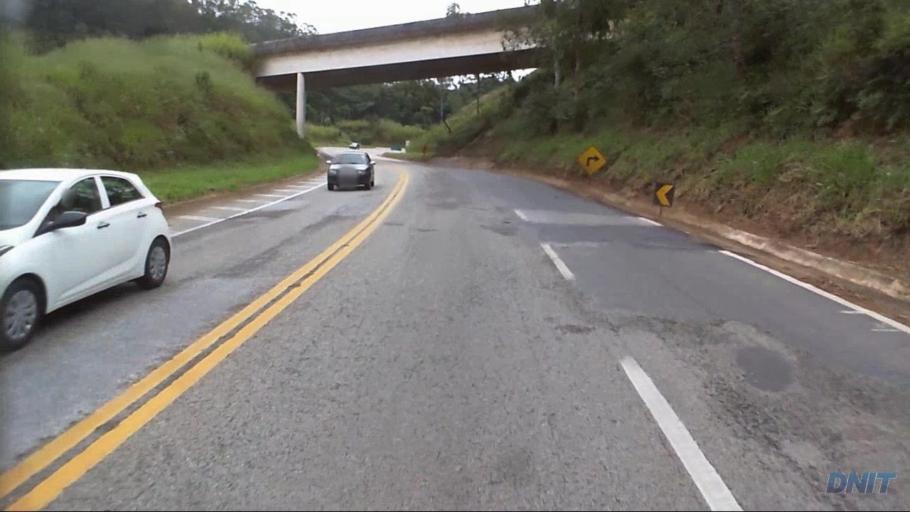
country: BR
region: Minas Gerais
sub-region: Joao Monlevade
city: Joao Monlevade
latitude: -19.8631
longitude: -43.1219
